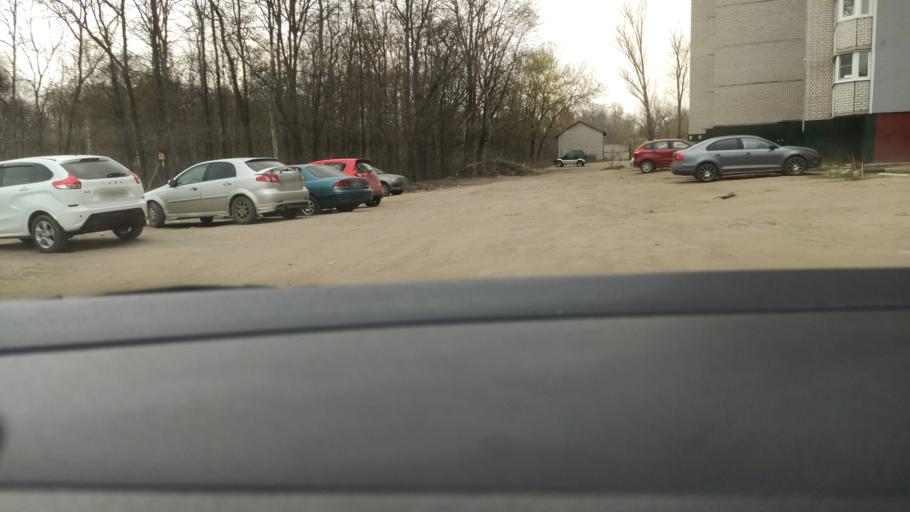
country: RU
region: Voronezj
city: Podgornoye
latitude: 51.7341
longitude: 39.1967
